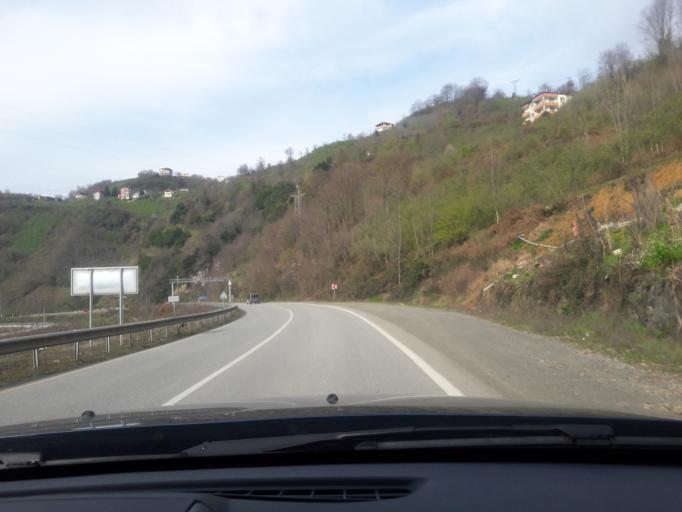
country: TR
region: Trabzon
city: Besikduzu
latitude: 41.0577
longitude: 39.2120
